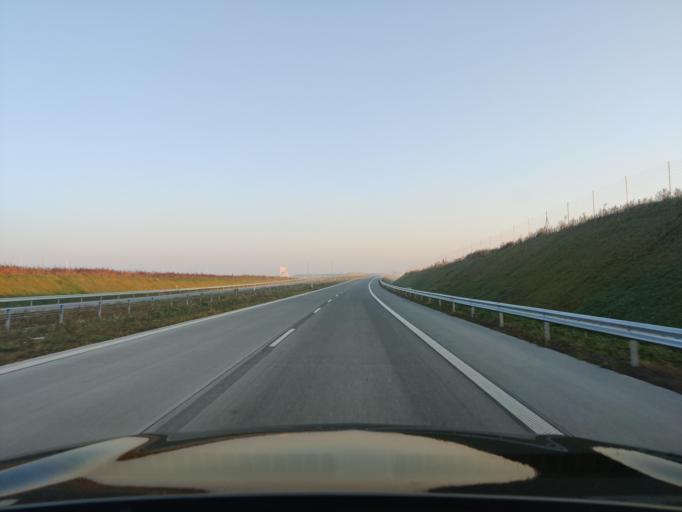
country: PL
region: Masovian Voivodeship
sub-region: Powiat mlawski
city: Mlawa
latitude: 53.1163
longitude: 20.4100
